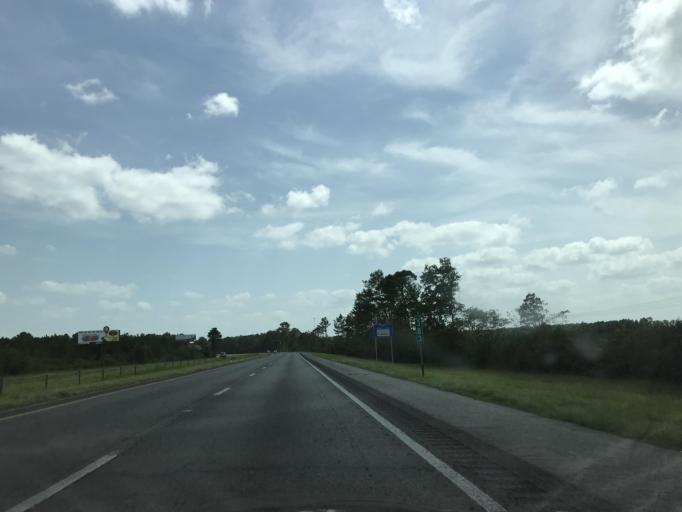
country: US
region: North Carolina
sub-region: Duplin County
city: Wallace
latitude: 34.7824
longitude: -77.9749
